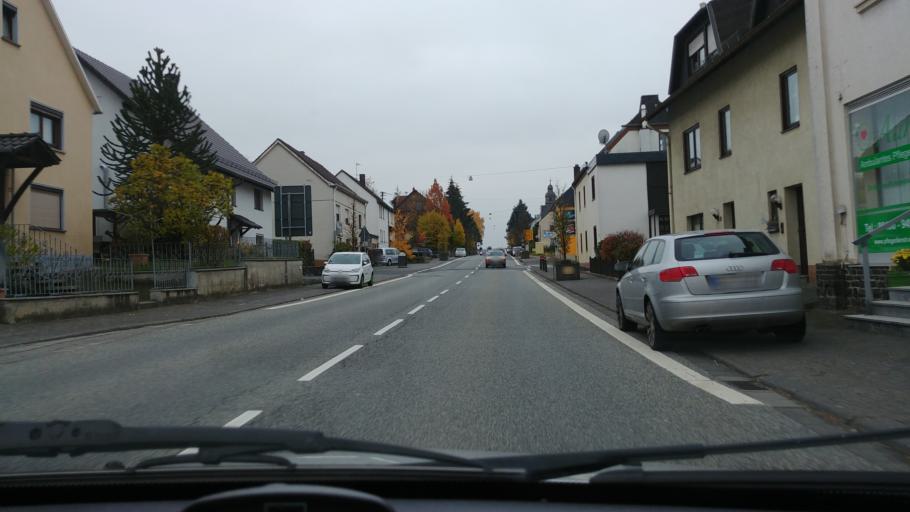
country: DE
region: Rheinland-Pfalz
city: Irmtraut
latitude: 50.5381
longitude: 8.0484
